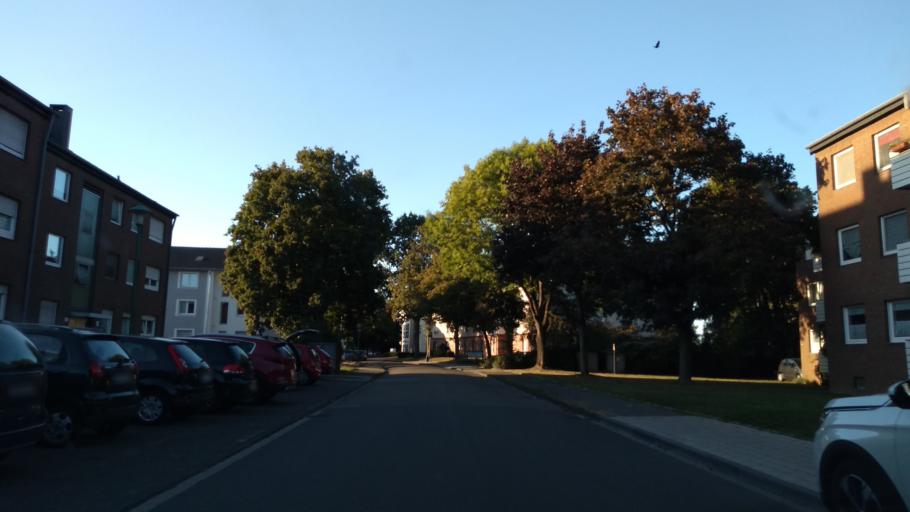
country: DE
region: North Rhine-Westphalia
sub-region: Regierungsbezirk Dusseldorf
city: Dinslaken
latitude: 51.5498
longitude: 6.7180
